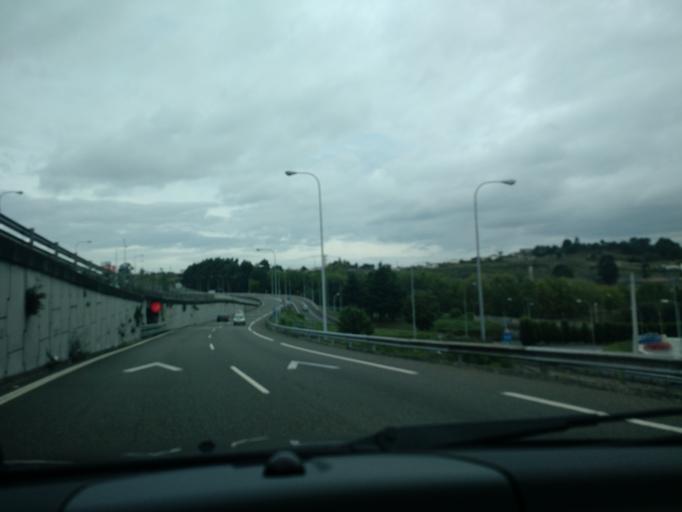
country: ES
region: Galicia
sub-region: Provincia da Coruna
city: Culleredo
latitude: 43.3280
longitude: -8.3963
